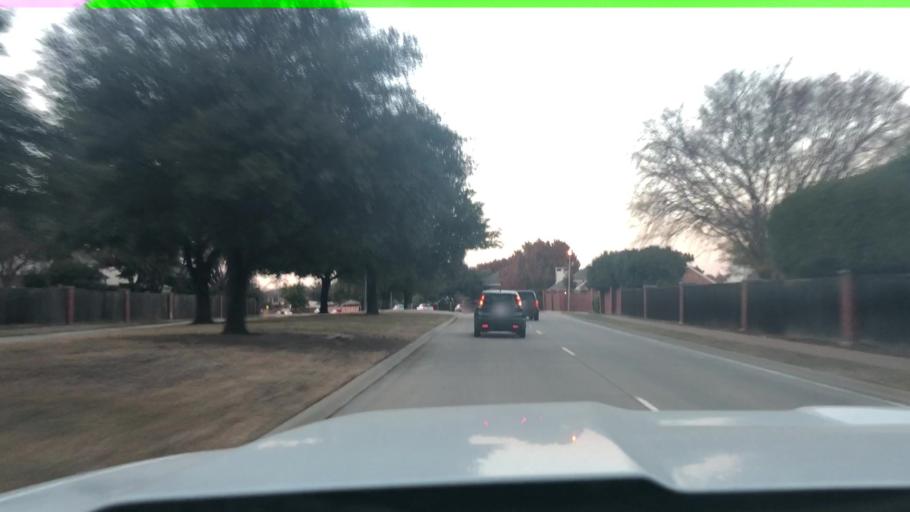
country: US
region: Texas
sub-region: Denton County
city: Flower Mound
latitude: 33.0192
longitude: -97.0759
